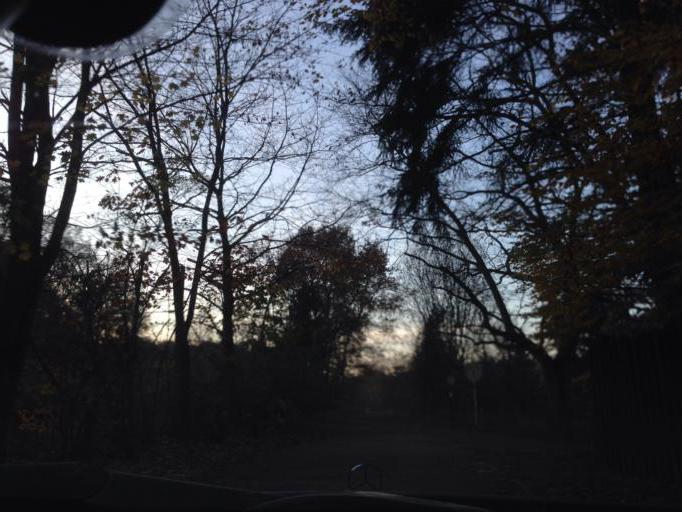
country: DE
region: Schleswig-Holstein
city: Aumuhle
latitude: 53.5294
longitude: 10.3330
